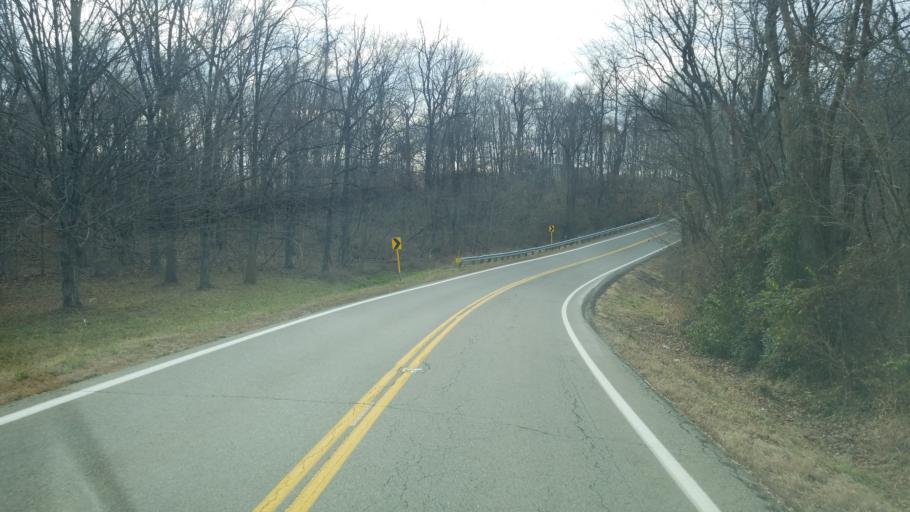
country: US
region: Ohio
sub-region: Ross County
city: Frankfort
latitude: 39.3512
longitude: -83.1675
